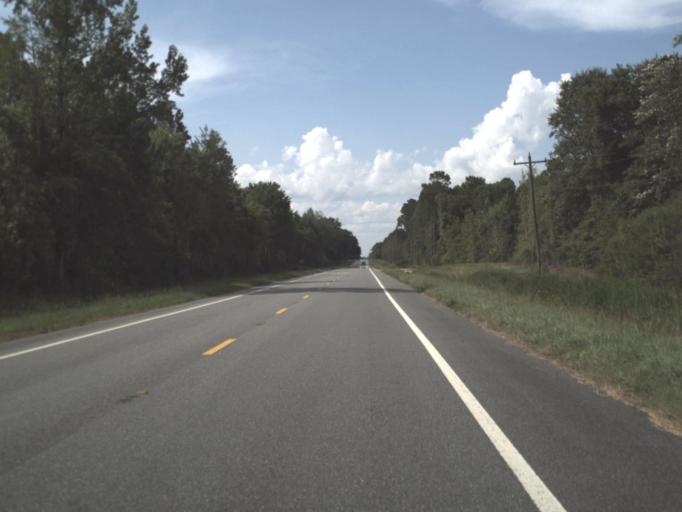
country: US
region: Florida
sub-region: Taylor County
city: Perry
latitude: 30.2417
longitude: -83.6201
